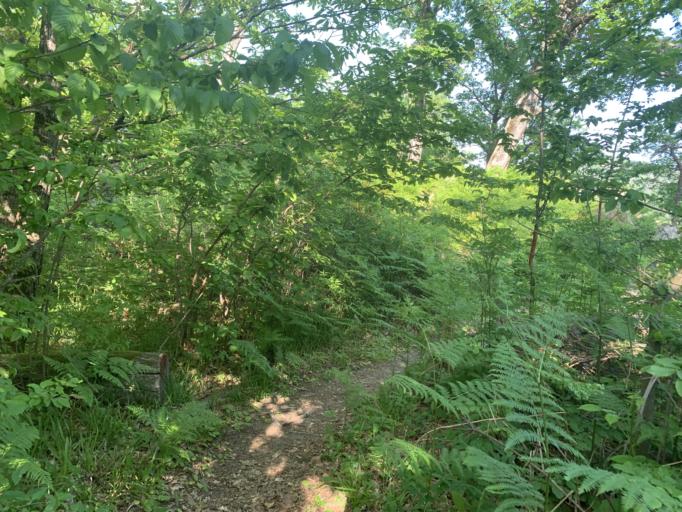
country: RU
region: Krasnodarskiy
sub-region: Sochi City
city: Lazarevskoye
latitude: 43.9510
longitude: 39.3293
